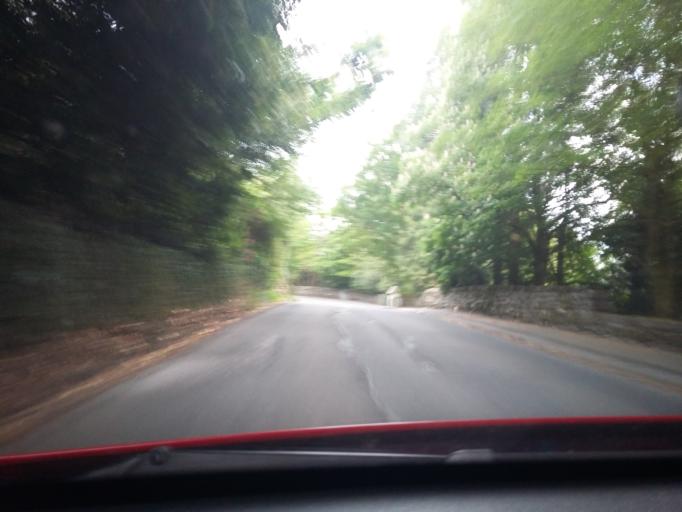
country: GB
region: England
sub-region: Cumbria
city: Windermere
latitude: 54.3917
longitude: -2.9147
